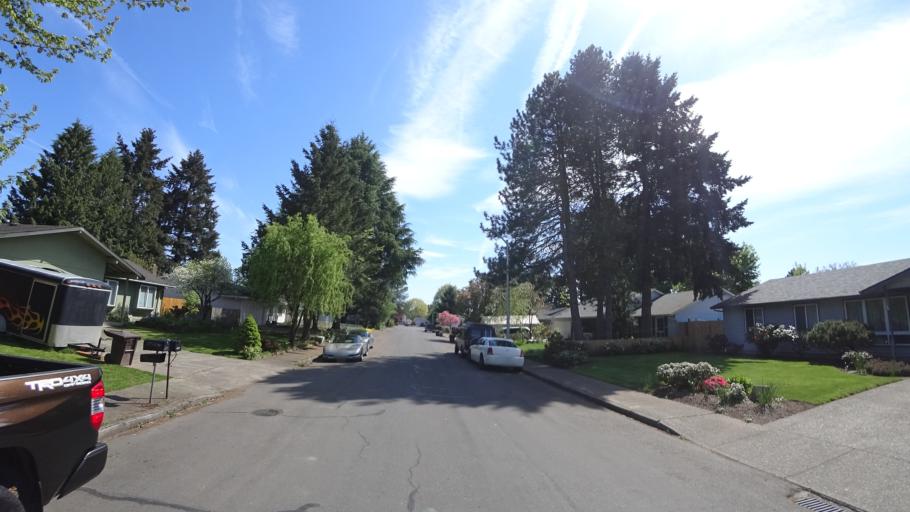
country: US
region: Oregon
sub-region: Washington County
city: Hillsboro
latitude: 45.5186
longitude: -122.9488
